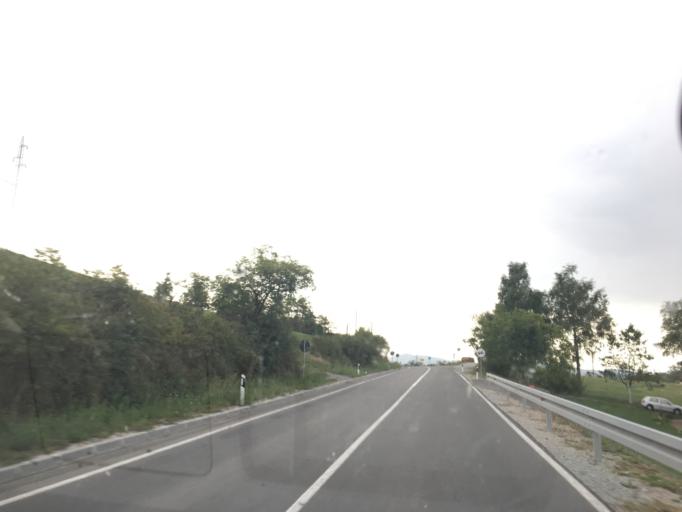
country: RS
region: Central Serbia
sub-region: Moravicki Okrug
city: Gornji Milanovac
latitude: 44.1349
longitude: 20.4932
